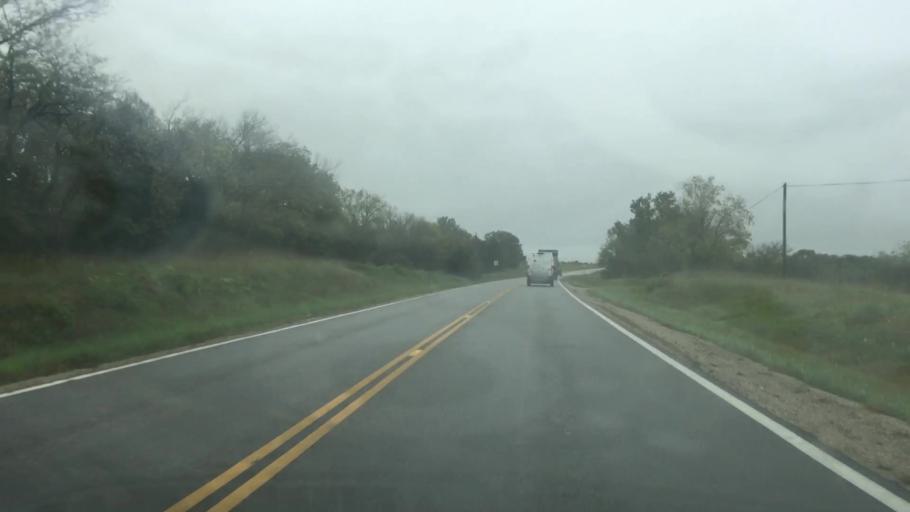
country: US
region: Kansas
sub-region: Anderson County
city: Garnett
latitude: 38.2018
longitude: -95.2495
